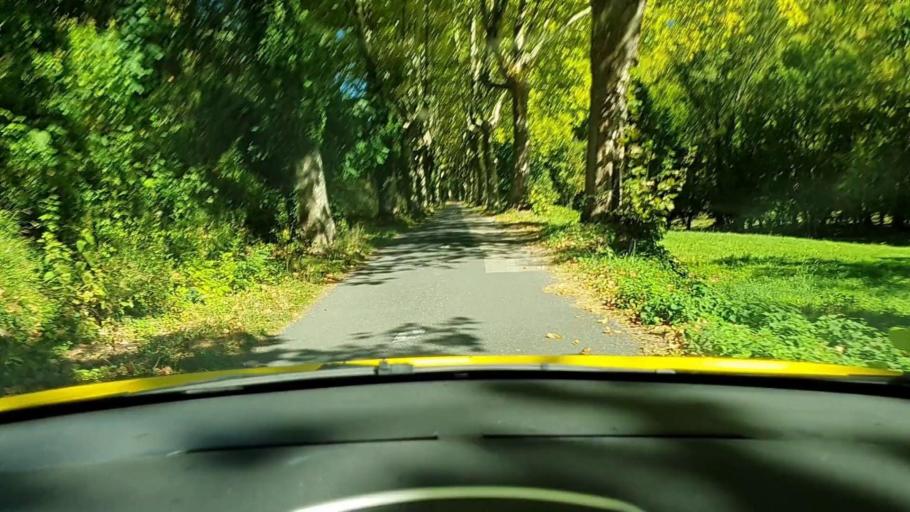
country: FR
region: Languedoc-Roussillon
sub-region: Departement du Gard
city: Le Vigan
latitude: 43.9737
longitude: 3.4386
